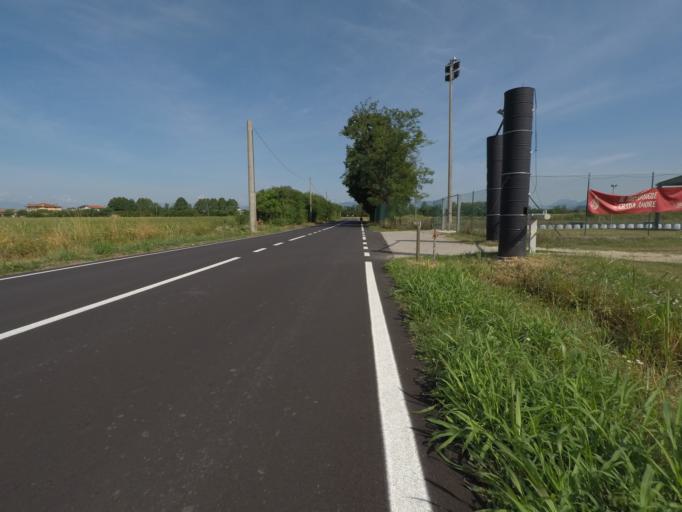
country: IT
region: Friuli Venezia Giulia
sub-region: Provincia di Udine
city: San Vito di Fagagna
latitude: 46.0675
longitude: 13.0882
